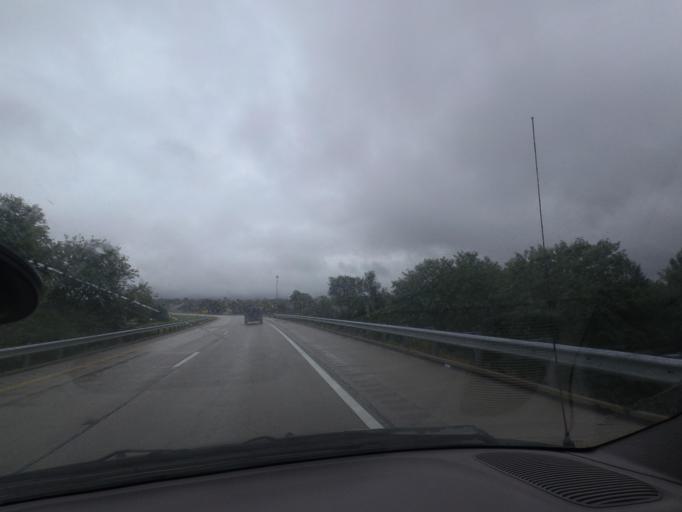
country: US
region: Illinois
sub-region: Champaign County
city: Champaign
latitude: 40.1175
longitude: -88.2864
